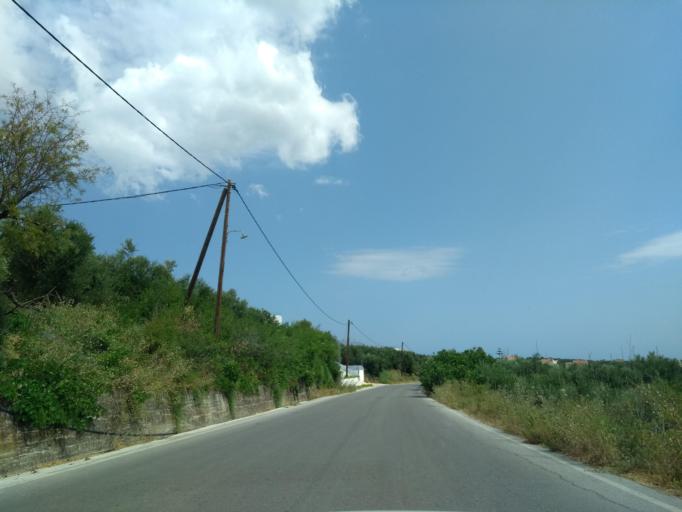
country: GR
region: Crete
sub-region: Nomos Chanias
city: Kalivai
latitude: 35.4405
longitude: 24.1754
